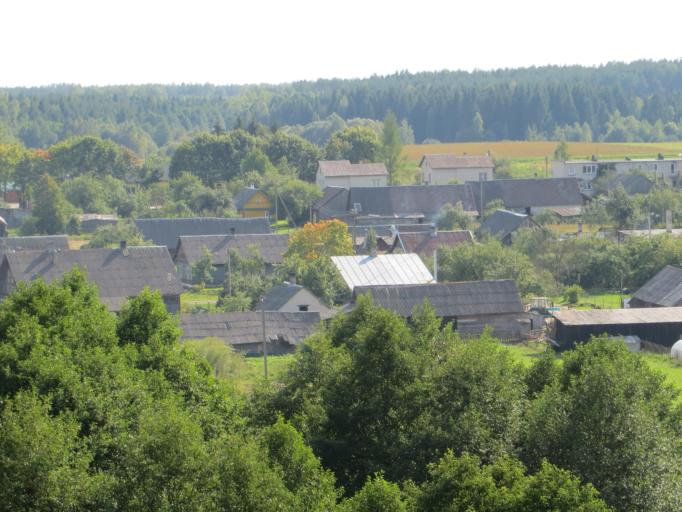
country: LT
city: Salcininkai
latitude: 54.2918
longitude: 25.2158
